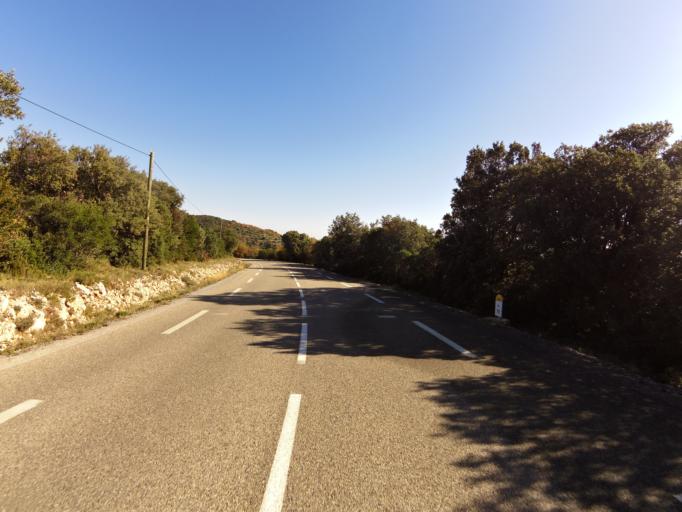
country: FR
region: Rhone-Alpes
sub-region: Departement de l'Ardeche
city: Ruoms
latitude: 44.3992
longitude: 4.4732
